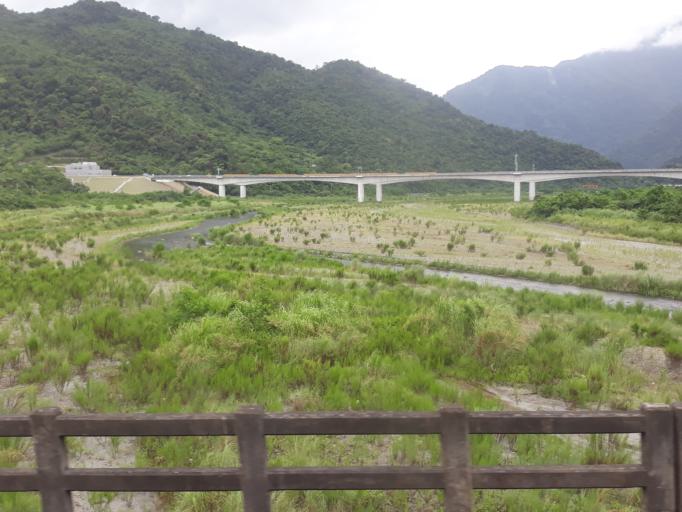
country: TW
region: Taiwan
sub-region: Yilan
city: Yilan
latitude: 24.4409
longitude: 121.7800
